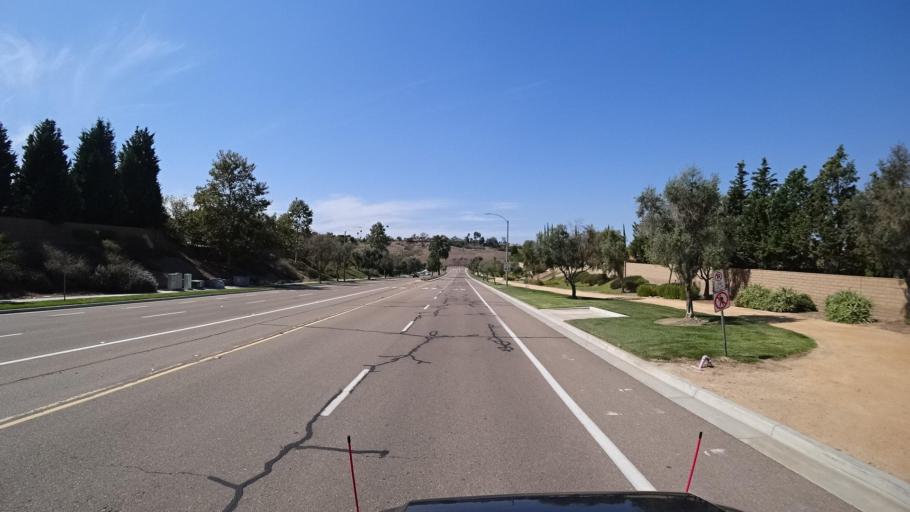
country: US
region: California
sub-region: San Diego County
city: La Presa
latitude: 32.6727
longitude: -116.9944
